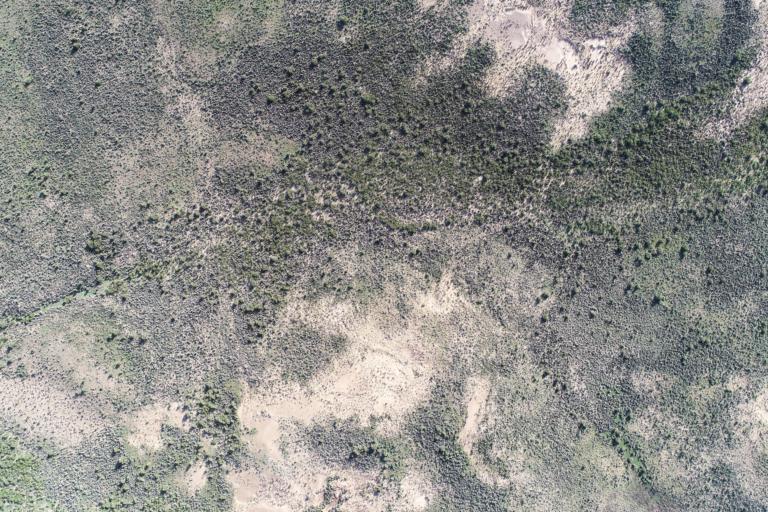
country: BO
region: La Paz
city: Curahuara de Carangas
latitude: -17.2991
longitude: -68.5130
